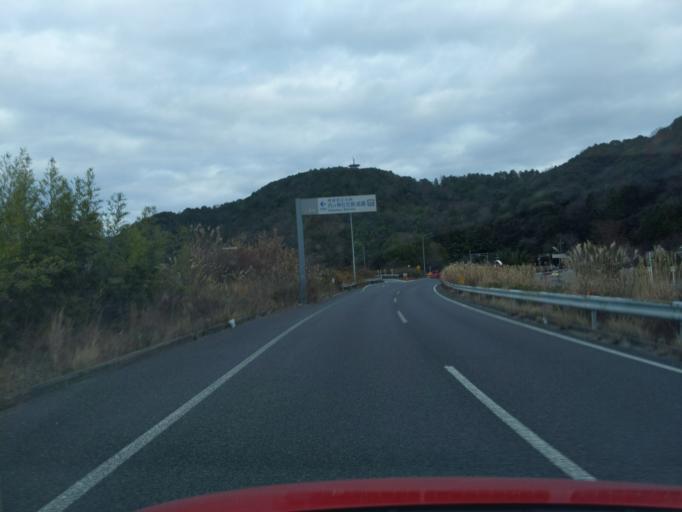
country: JP
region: Gifu
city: Tajimi
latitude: 35.3273
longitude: 137.0591
